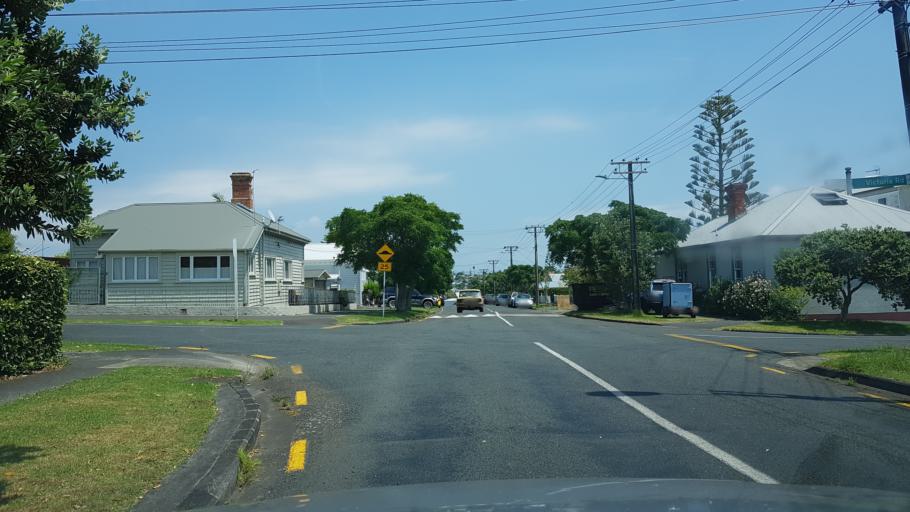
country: NZ
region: Auckland
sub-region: Auckland
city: North Shore
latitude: -36.8239
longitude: 174.7954
